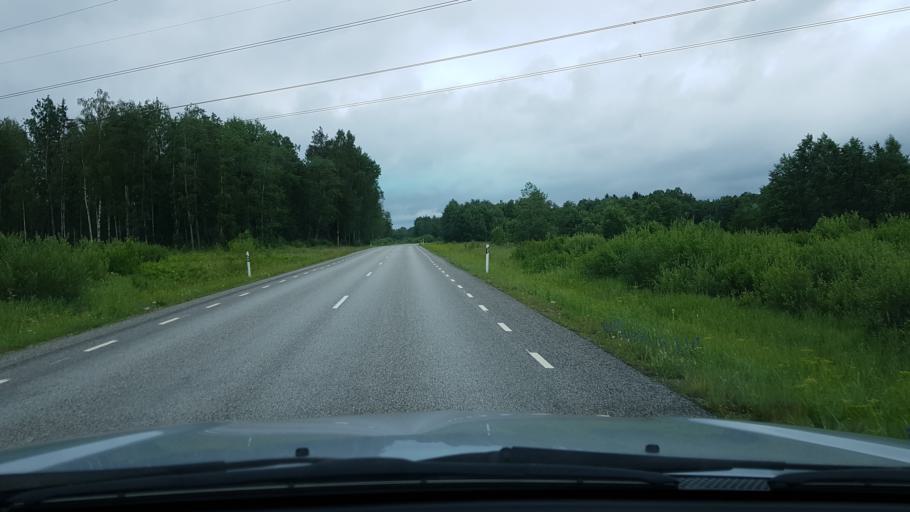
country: EE
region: Ida-Virumaa
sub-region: Narva-Joesuu linn
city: Narva-Joesuu
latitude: 59.3498
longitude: 27.9309
